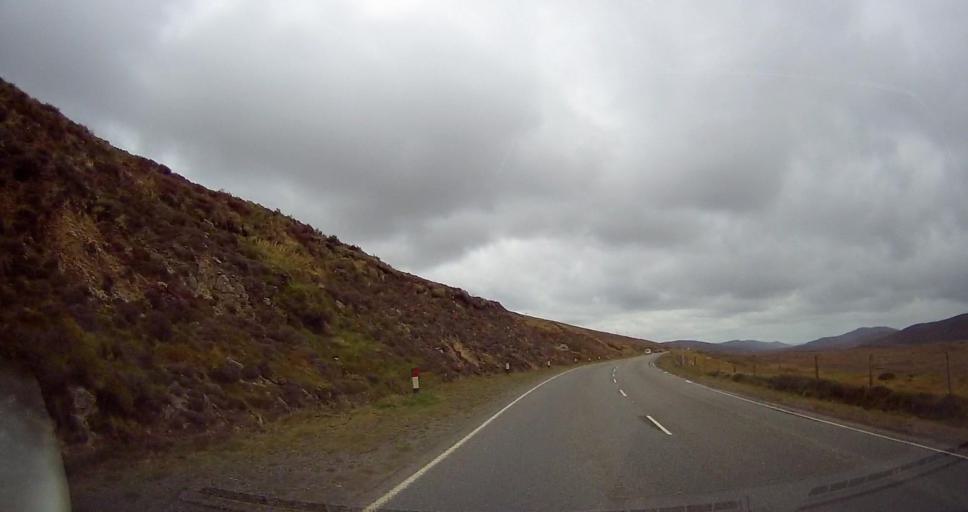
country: GB
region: Scotland
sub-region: Shetland Islands
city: Lerwick
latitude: 60.3044
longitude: -1.2392
